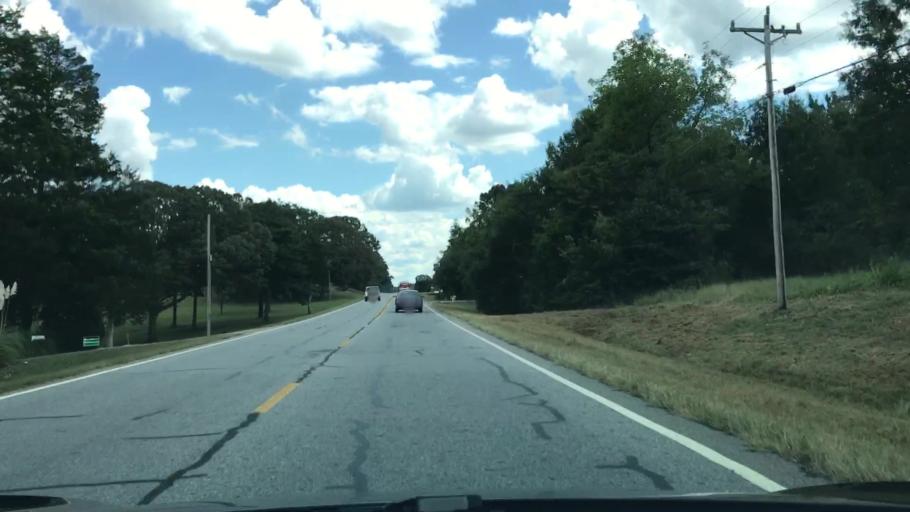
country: US
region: Georgia
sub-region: Oconee County
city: Watkinsville
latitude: 33.8012
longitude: -83.3384
